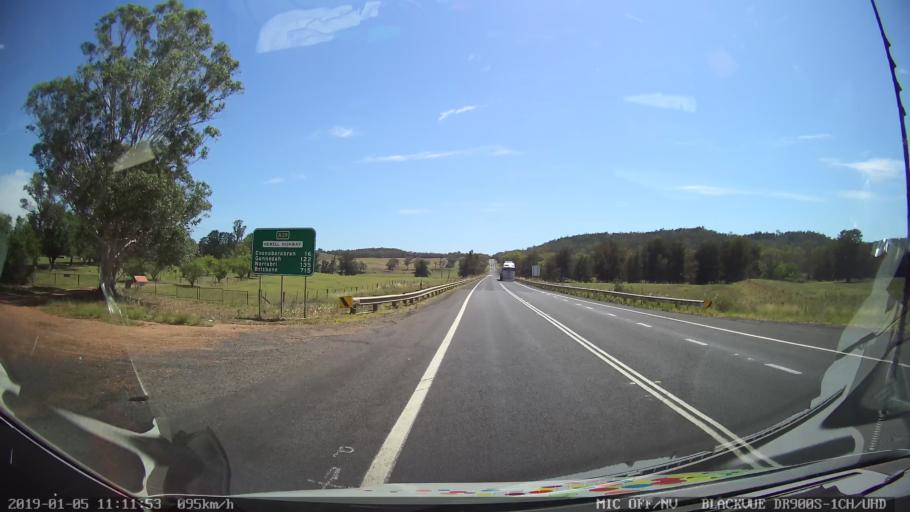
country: AU
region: New South Wales
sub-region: Warrumbungle Shire
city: Coonabarabran
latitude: -31.3878
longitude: 149.2545
